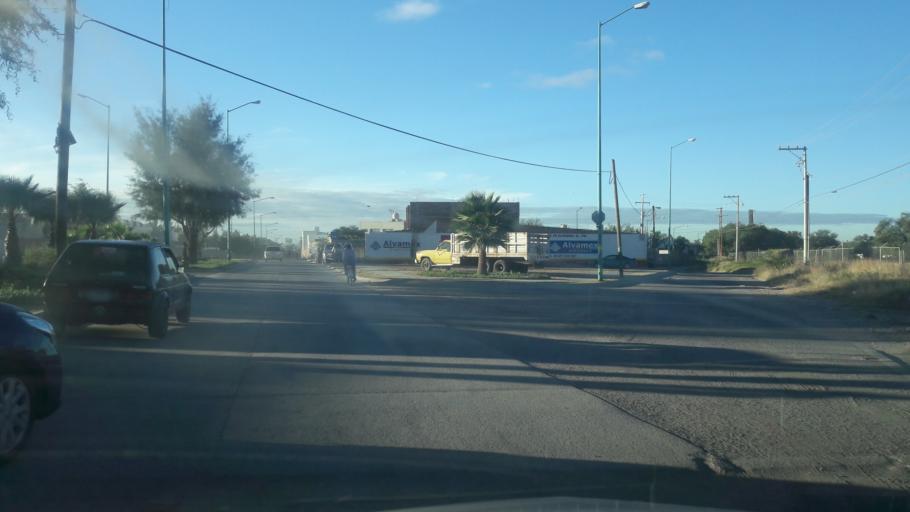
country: MX
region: Guanajuato
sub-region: Leon
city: Medina
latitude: 21.1634
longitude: -101.6425
